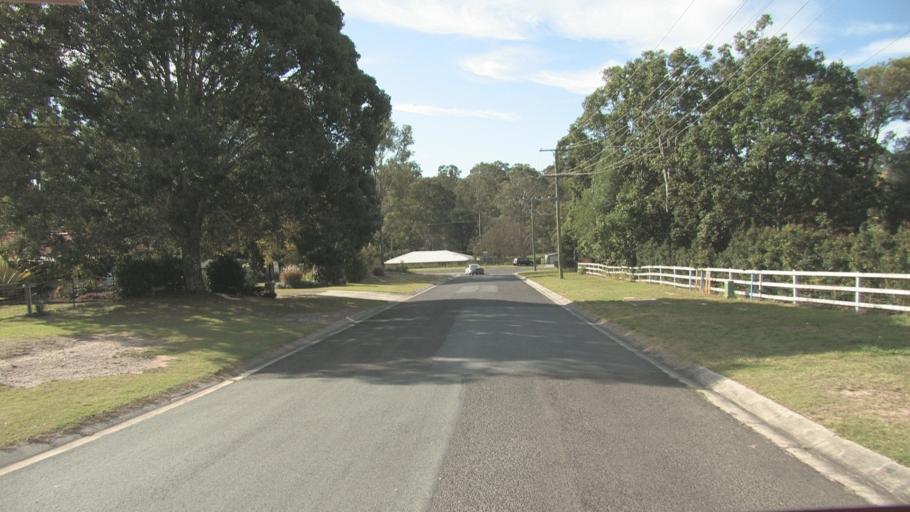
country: AU
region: Queensland
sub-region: Logan
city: Windaroo
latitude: -27.7650
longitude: 153.1889
